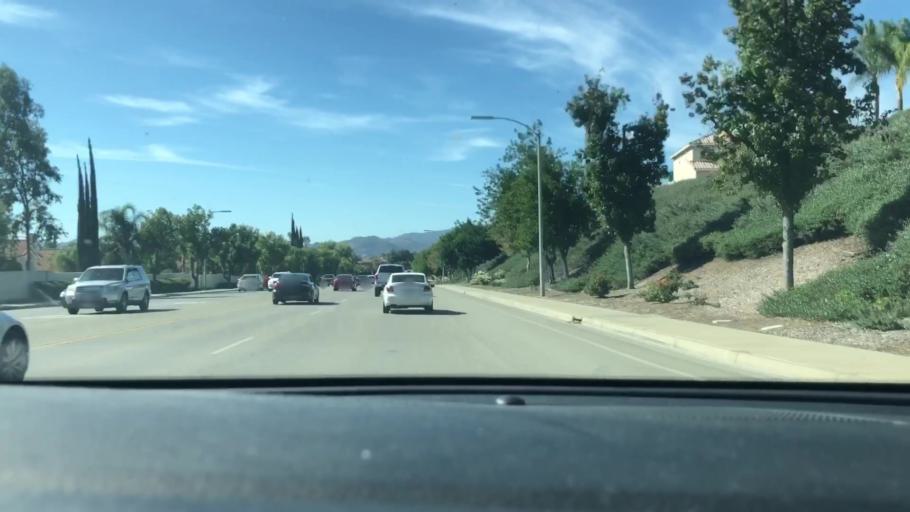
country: US
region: California
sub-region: Riverside County
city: Murrieta
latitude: 33.5962
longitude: -117.1910
